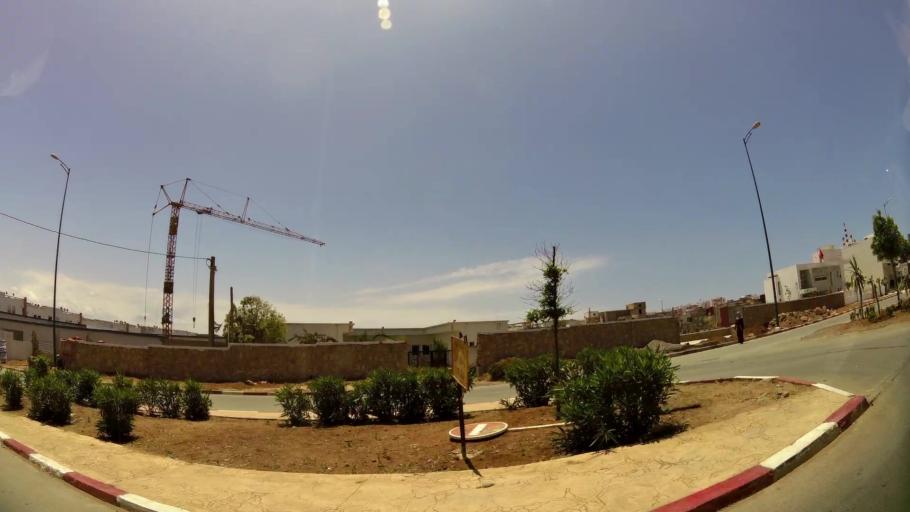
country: MA
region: Gharb-Chrarda-Beni Hssen
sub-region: Kenitra Province
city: Kenitra
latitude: 34.2568
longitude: -6.6509
